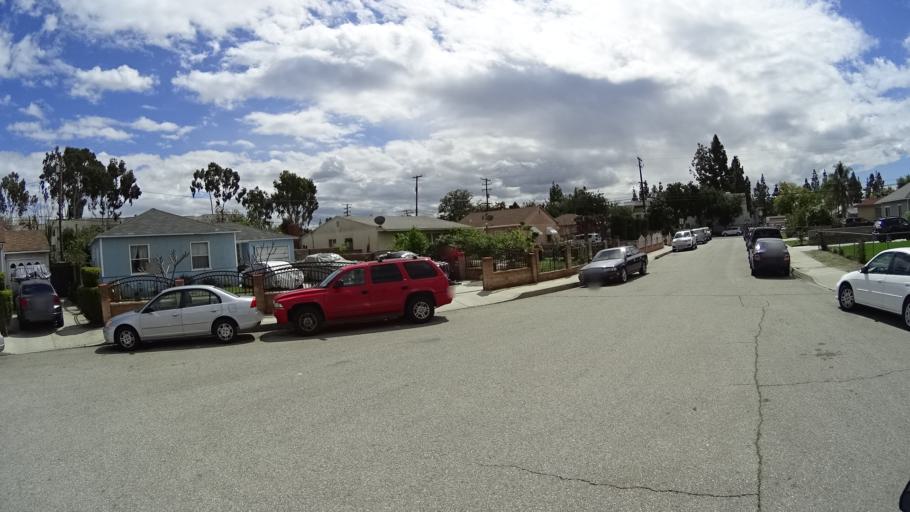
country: US
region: California
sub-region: Los Angeles County
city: Baldwin Park
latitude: 34.0911
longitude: -117.9631
